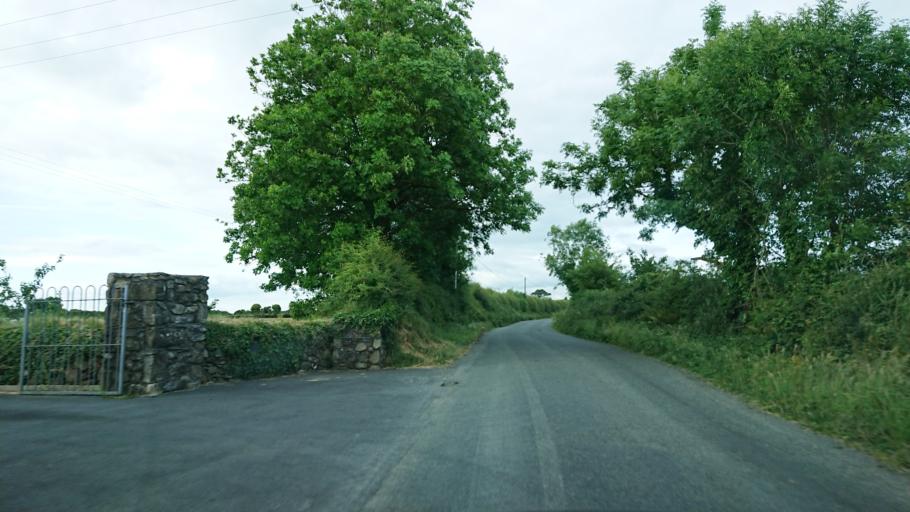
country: IE
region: Munster
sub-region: Waterford
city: Tra Mhor
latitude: 52.2090
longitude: -7.2083
